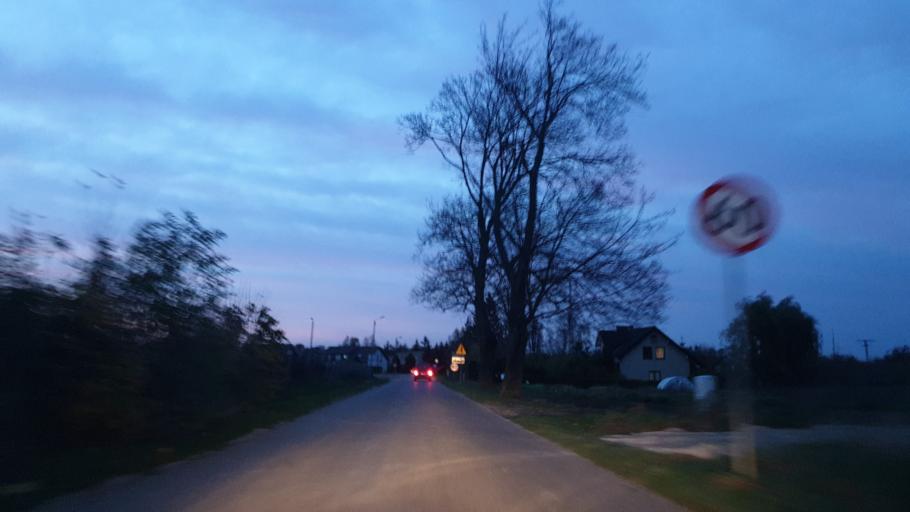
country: PL
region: Pomeranian Voivodeship
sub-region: Powiat pucki
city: Krokowa
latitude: 54.7827
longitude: 18.2003
